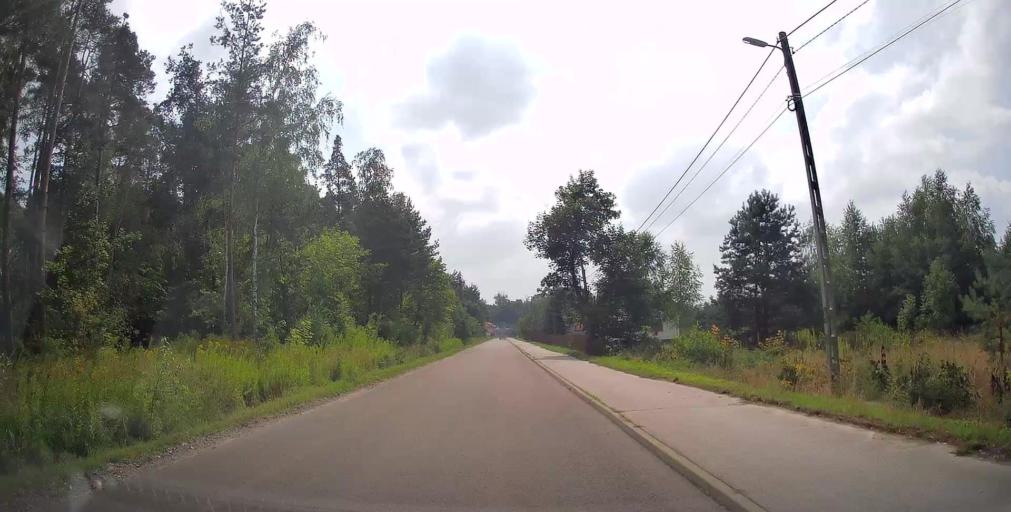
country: PL
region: Masovian Voivodeship
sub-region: Powiat bialobrzeski
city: Sucha
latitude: 51.6255
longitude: 20.9532
